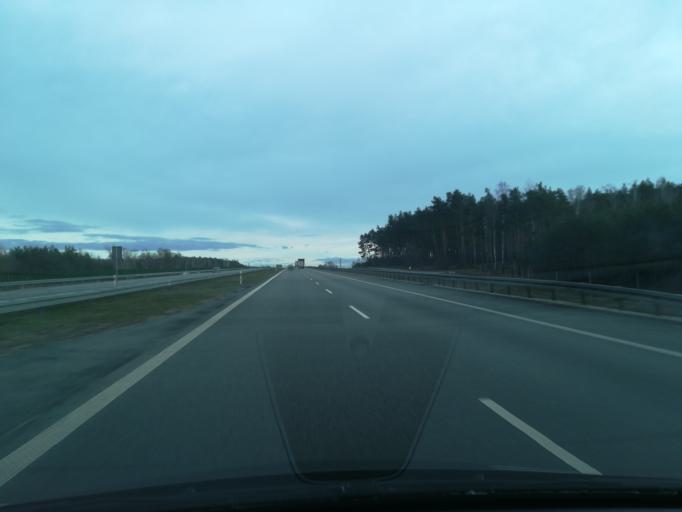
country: PL
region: Kujawsko-Pomorskie
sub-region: Powiat aleksandrowski
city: Ciechocinek
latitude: 52.8570
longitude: 18.7725
